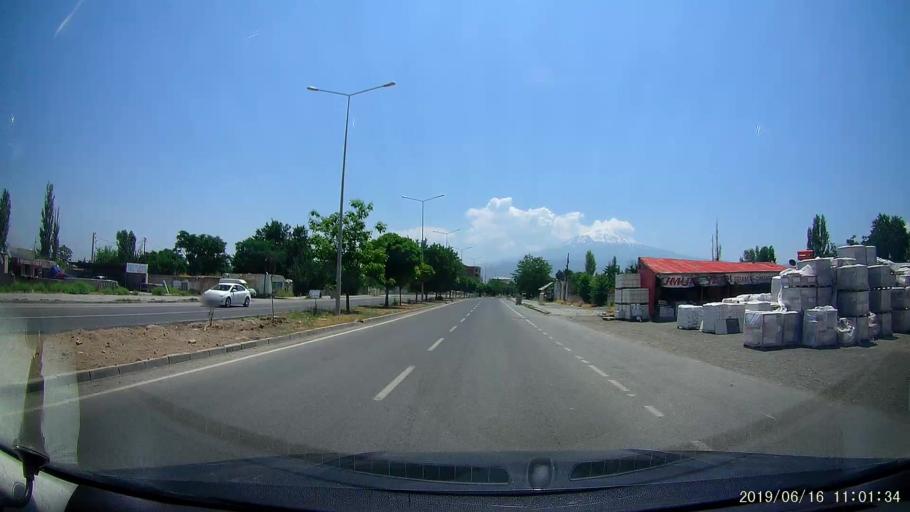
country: TR
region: Igdir
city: Igdir
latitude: 39.9142
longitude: 44.0510
